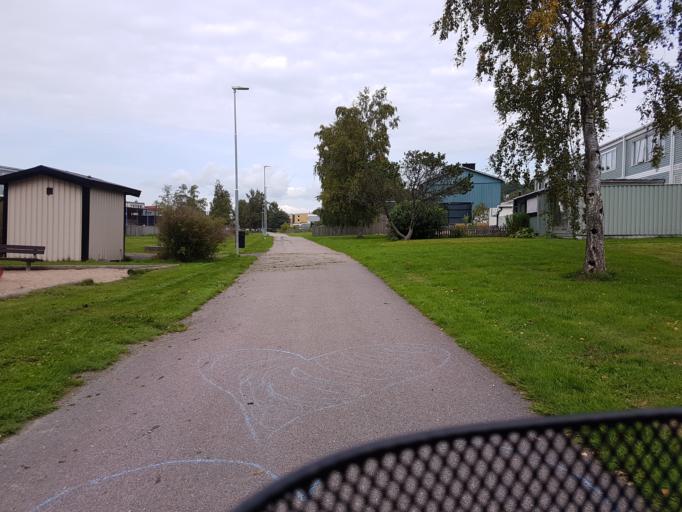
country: SE
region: Vaestra Goetaland
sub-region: Ale Kommun
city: Nodinge-Nol
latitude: 57.9104
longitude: 12.0685
